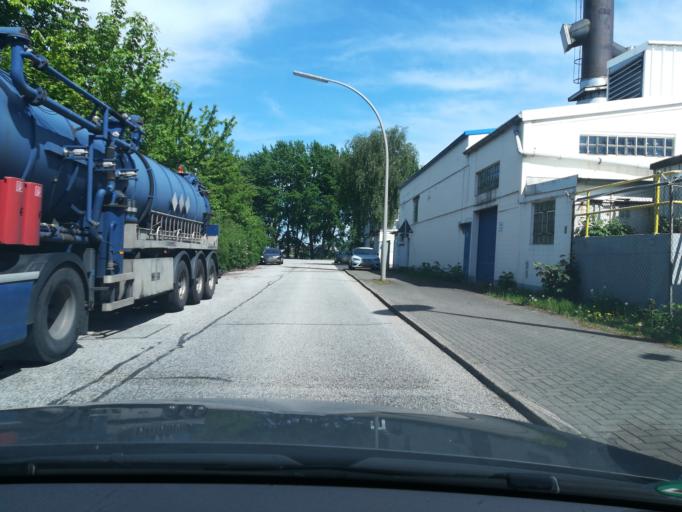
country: DE
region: Hamburg
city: Altona
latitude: 53.5062
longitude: 9.9485
